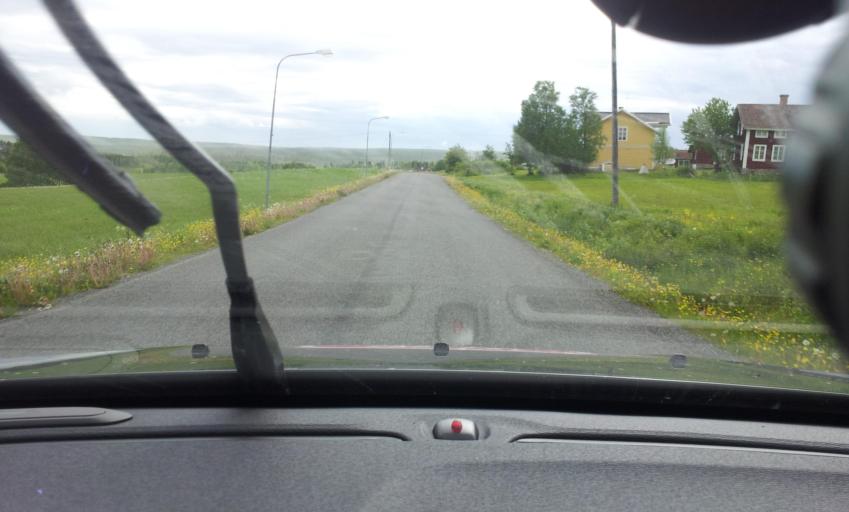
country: SE
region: Jaemtland
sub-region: OEstersunds Kommun
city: Brunflo
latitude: 63.0294
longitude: 14.8084
